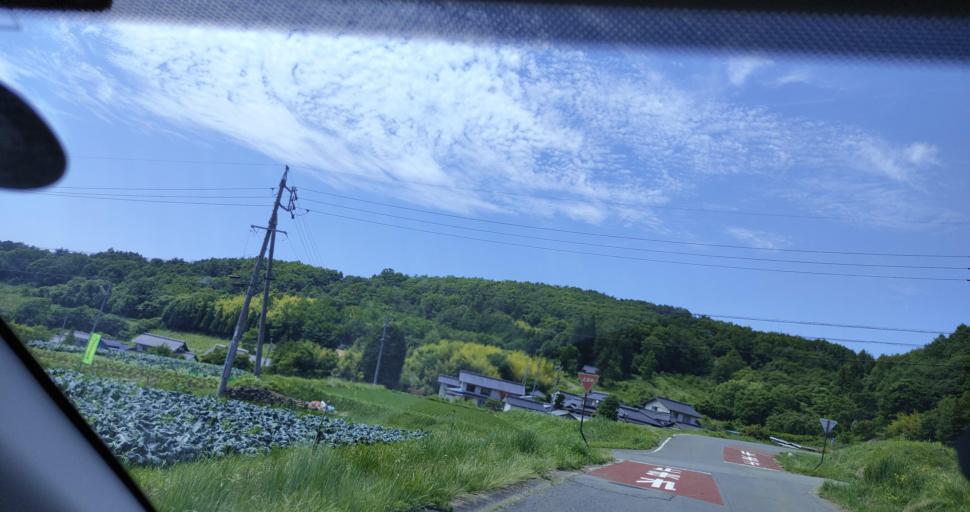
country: JP
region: Nagano
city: Ueda
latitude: 36.3914
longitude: 138.3329
